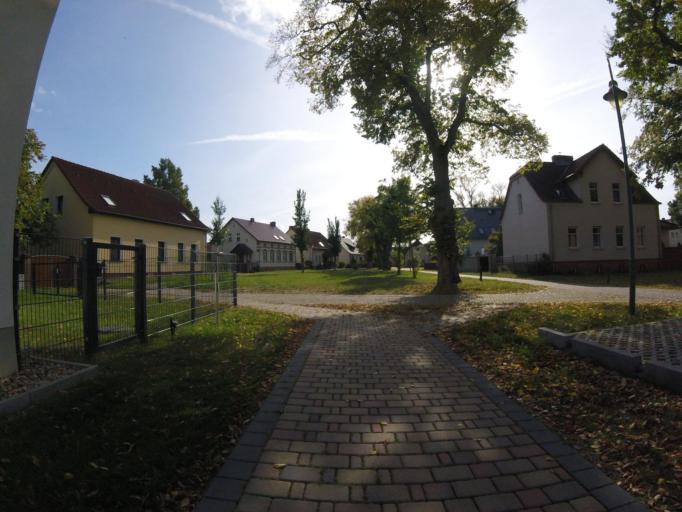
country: DE
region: Brandenburg
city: Bestensee
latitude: 52.2934
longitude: 13.7203
